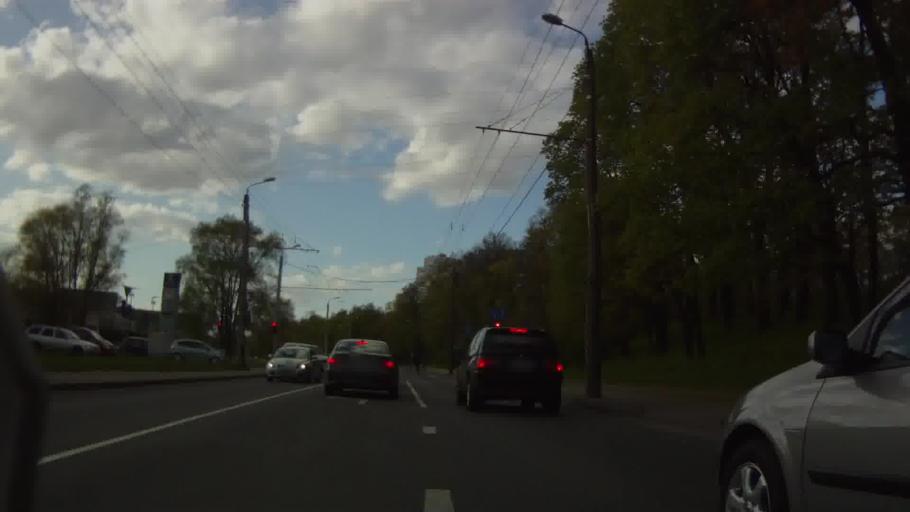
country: LV
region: Riga
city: Riga
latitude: 56.9845
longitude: 24.1355
